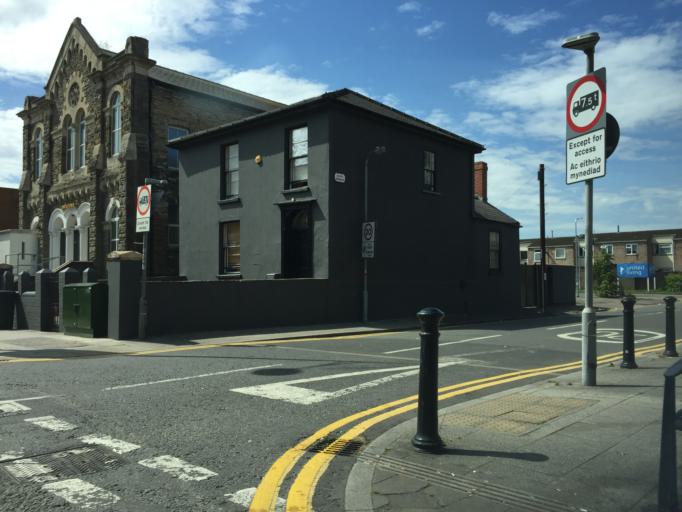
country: GB
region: Wales
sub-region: Newport
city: Newport
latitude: 51.5802
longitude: -2.9909
